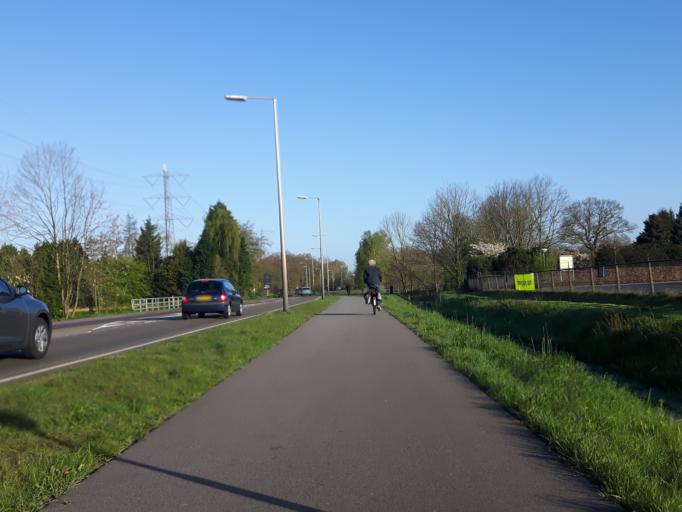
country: NL
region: Overijssel
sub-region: Gemeente Enschede
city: Enschede
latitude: 52.2070
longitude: 6.8521
